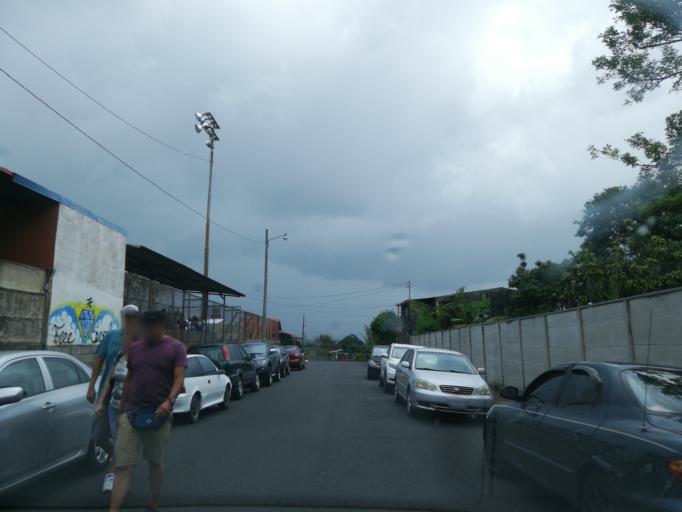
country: CR
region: Alajuela
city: Alajuela
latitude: 10.0327
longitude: -84.2011
